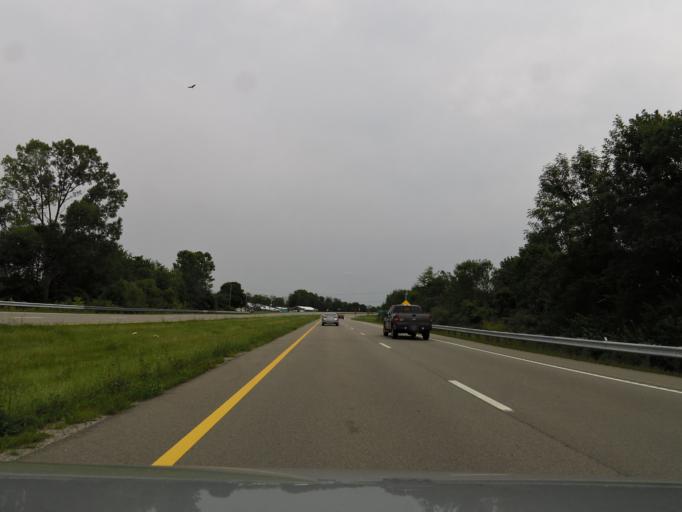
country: US
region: Ohio
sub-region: Warren County
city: Waynesville
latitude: 39.4991
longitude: -84.0033
